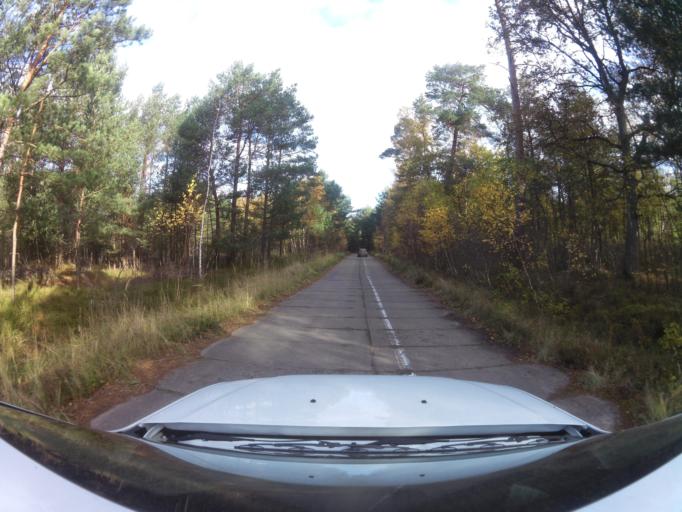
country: PL
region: West Pomeranian Voivodeship
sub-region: Powiat gryficki
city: Cerkwica
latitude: 54.0996
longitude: 15.1406
